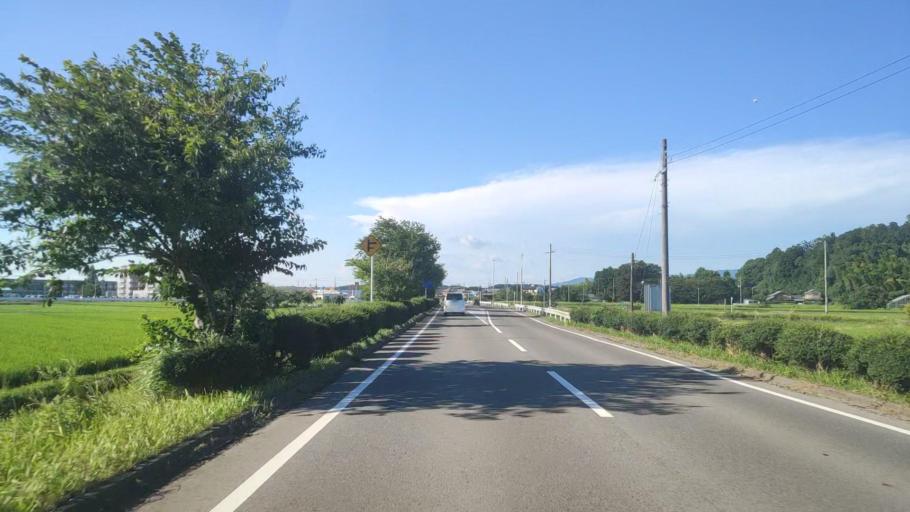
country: JP
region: Shiga Prefecture
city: Hino
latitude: 35.0079
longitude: 136.2396
